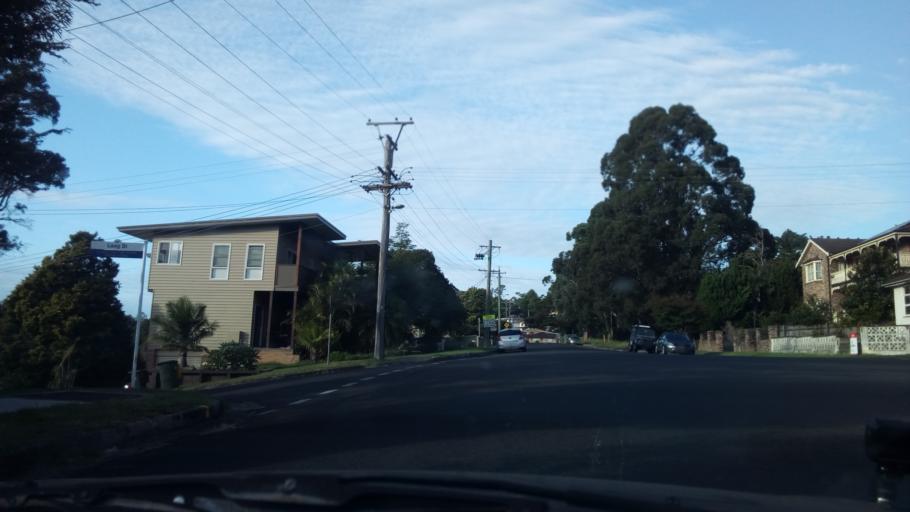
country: AU
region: New South Wales
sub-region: Wollongong
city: Mount Ousley
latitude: -34.3858
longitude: 150.8729
